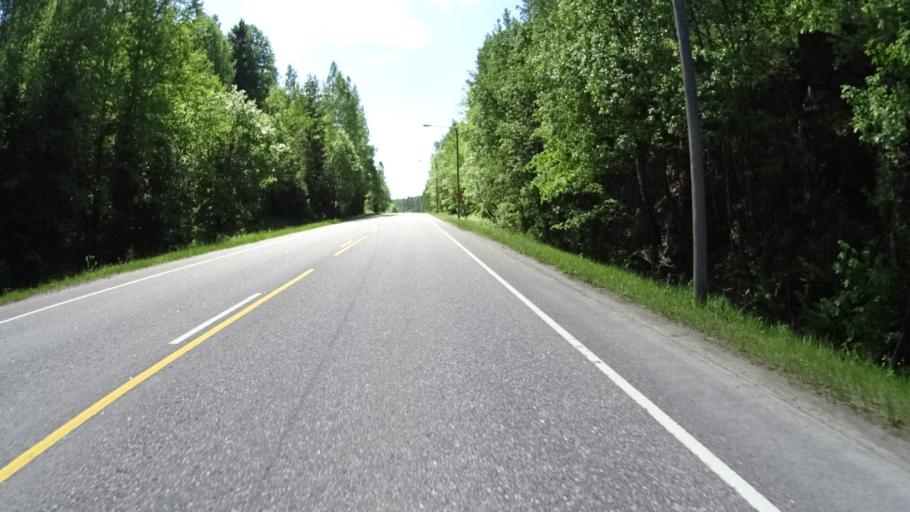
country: FI
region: Uusimaa
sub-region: Helsinki
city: Nurmijaervi
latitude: 60.3768
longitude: 24.8062
